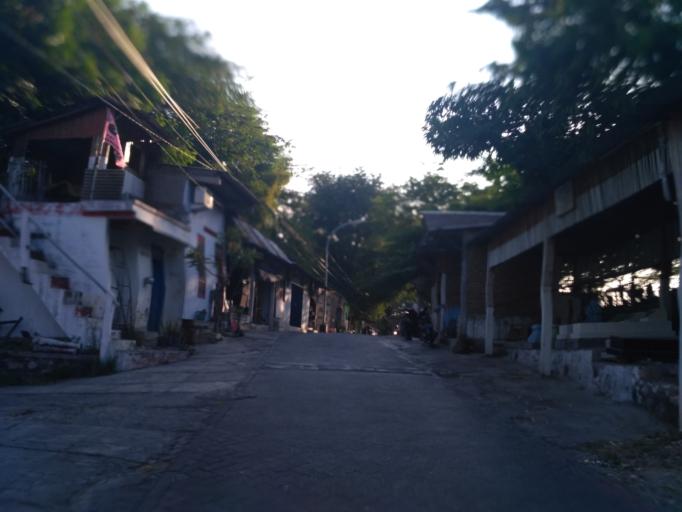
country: ID
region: Central Java
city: Semarang
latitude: -6.9913
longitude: 110.4094
